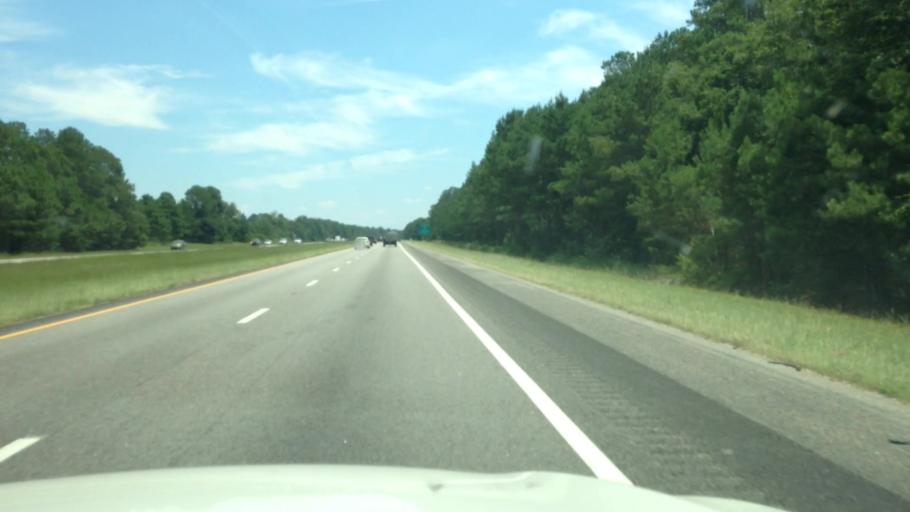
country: US
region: South Carolina
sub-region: Florence County
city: Timmonsville
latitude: 34.2032
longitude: -79.8900
